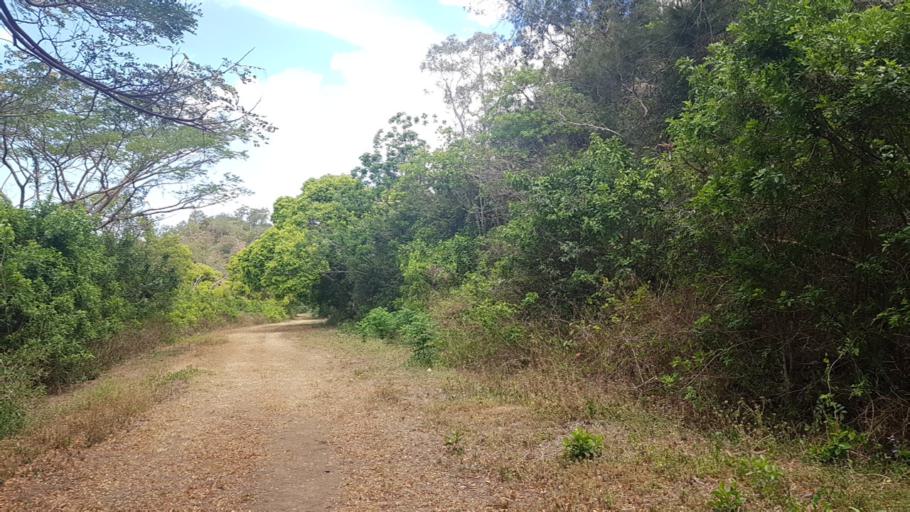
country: NC
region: South Province
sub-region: Dumbea
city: Dumbea
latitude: -22.1764
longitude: 166.4760
